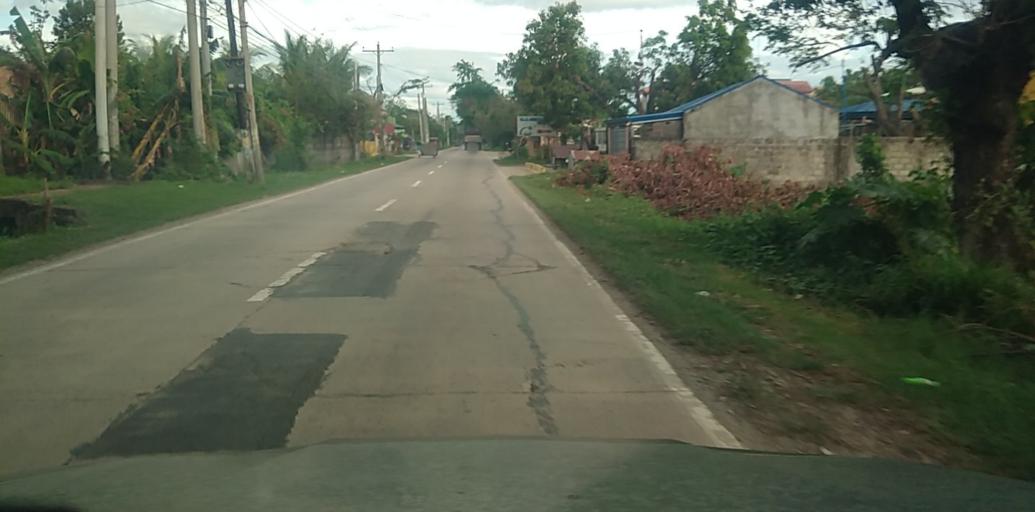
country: PH
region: Central Luzon
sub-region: Province of Pampanga
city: Arayat
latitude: 15.1530
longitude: 120.7337
